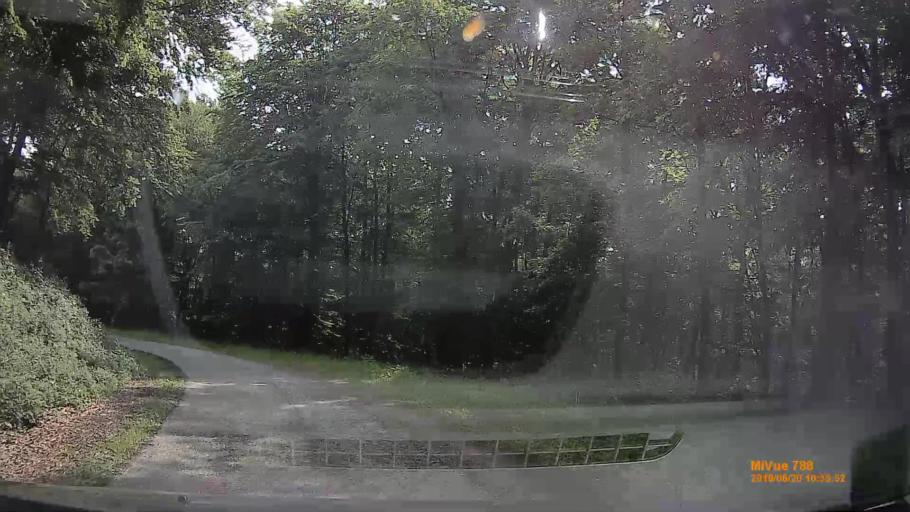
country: HU
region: Baranya
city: Mecseknadasd
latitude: 46.2011
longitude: 18.5271
